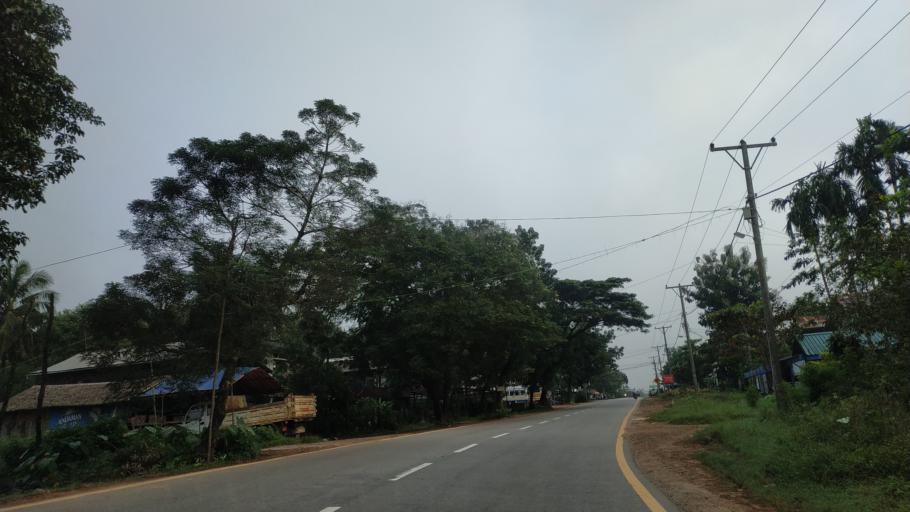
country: MM
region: Tanintharyi
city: Dawei
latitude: 14.1562
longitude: 98.2033
